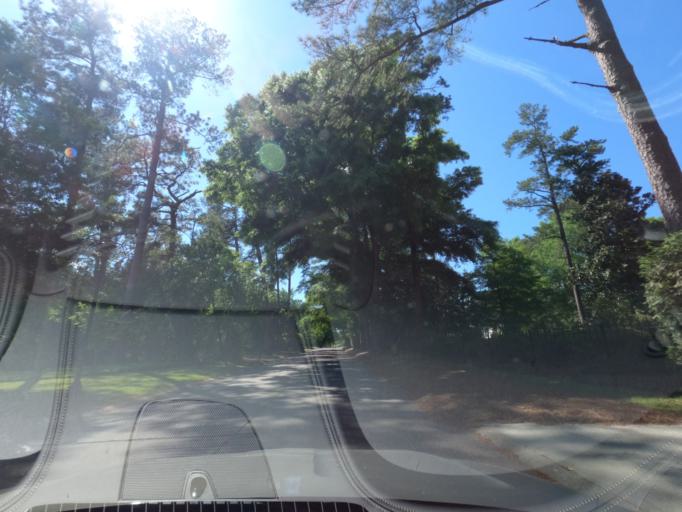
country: US
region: Georgia
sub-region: Columbia County
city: Martinez
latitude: 33.4728
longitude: -82.0440
